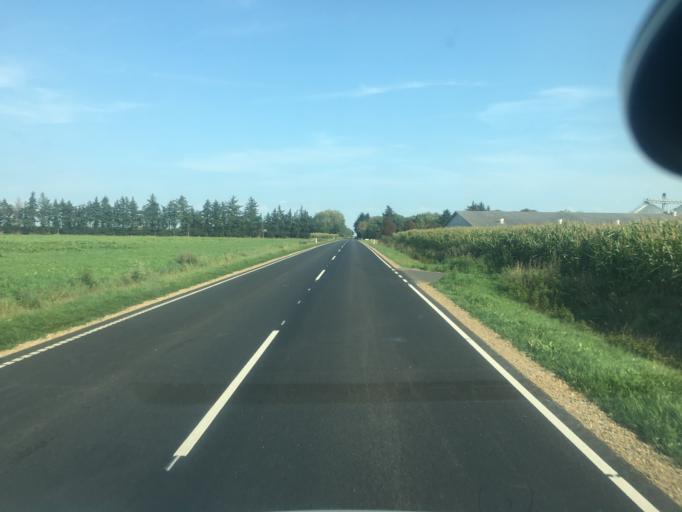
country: DK
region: South Denmark
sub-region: Tonder Kommune
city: Logumkloster
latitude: 54.9998
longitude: 8.9209
